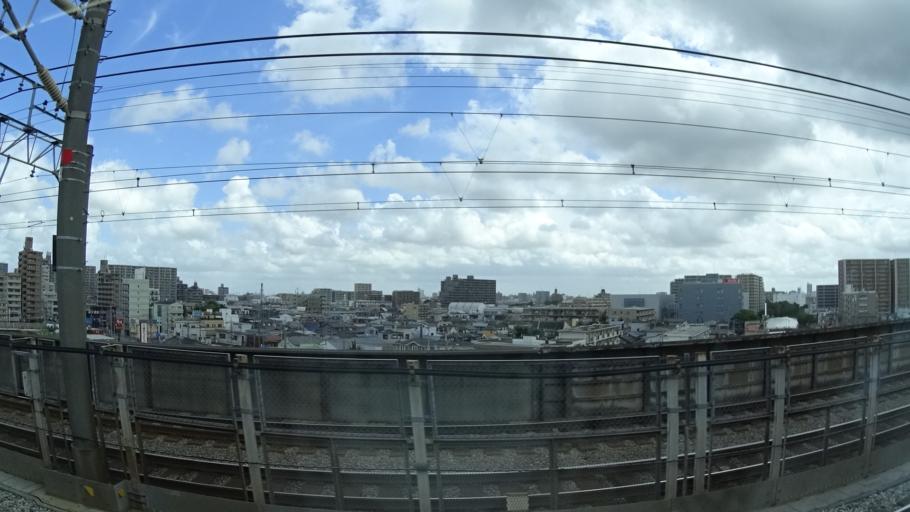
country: JP
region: Saitama
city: Shimotoda
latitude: 35.8065
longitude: 139.6799
